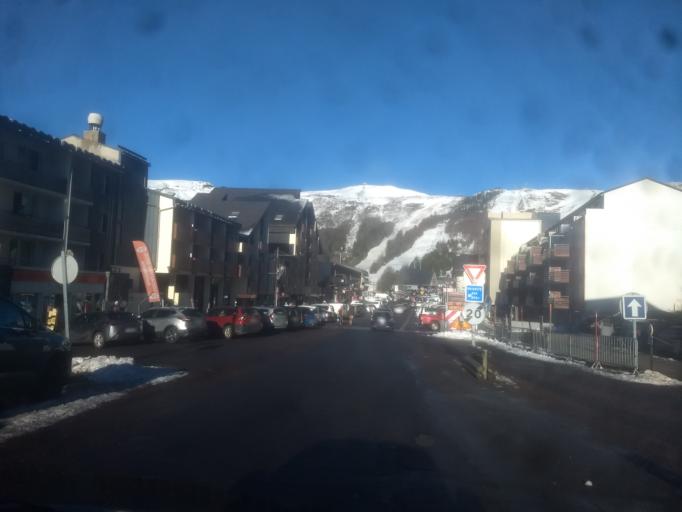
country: FR
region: Auvergne
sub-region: Departement du Puy-de-Dome
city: Mont-Dore
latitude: 45.5106
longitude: 2.8571
